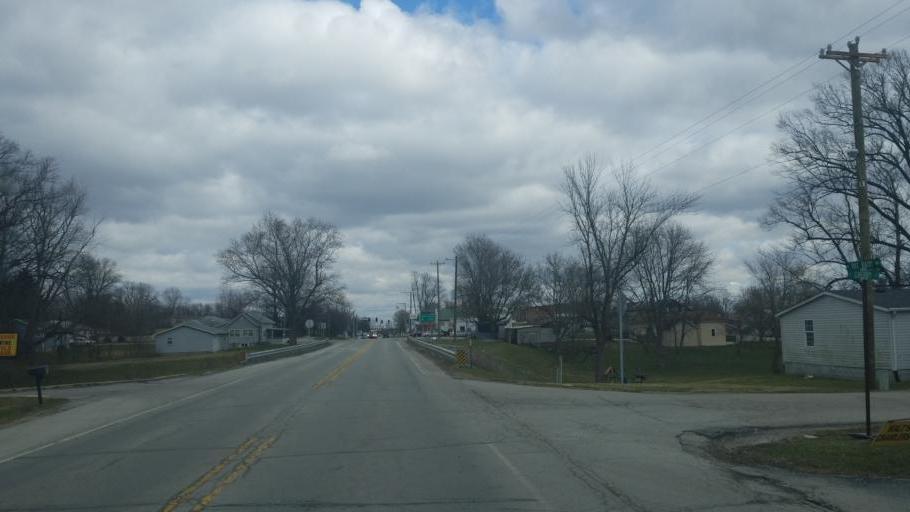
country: US
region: Indiana
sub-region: Putnam County
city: Greencastle
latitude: 39.7620
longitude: -86.8148
